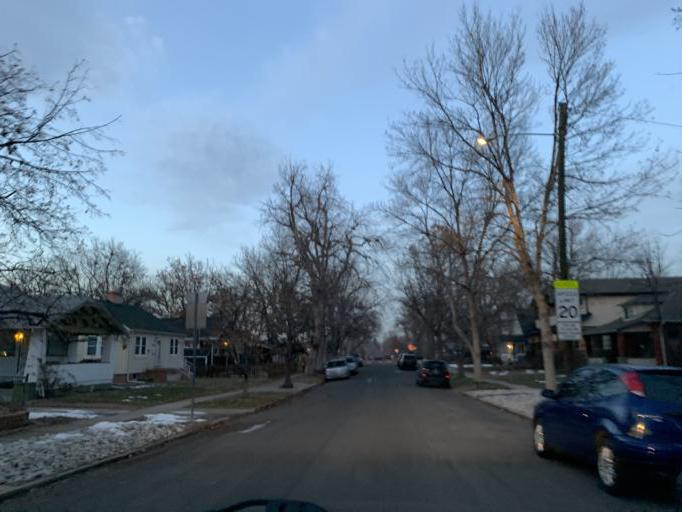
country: US
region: Colorado
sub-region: Adams County
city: Berkley
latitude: 39.7792
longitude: -105.0416
